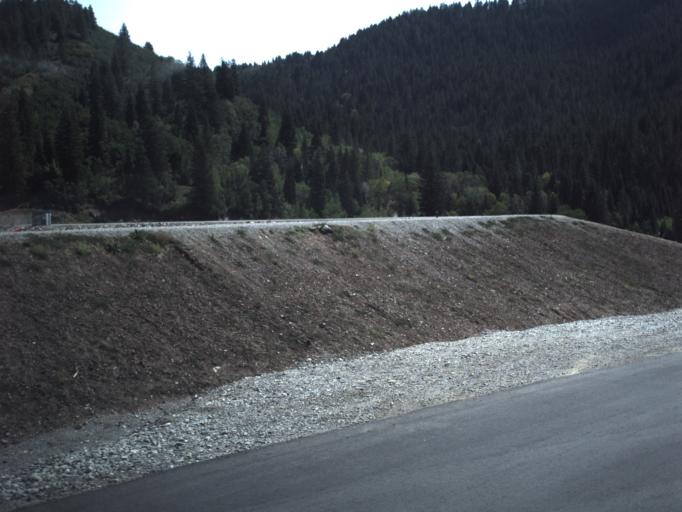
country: US
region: Utah
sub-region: Utah County
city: Highland
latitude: 40.4815
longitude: -111.6474
